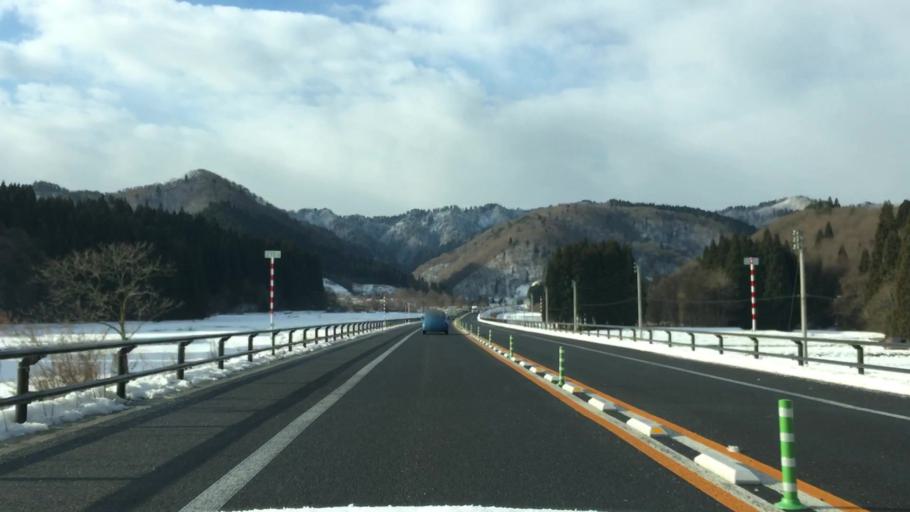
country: JP
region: Akita
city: Odate
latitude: 40.2355
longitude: 140.4992
